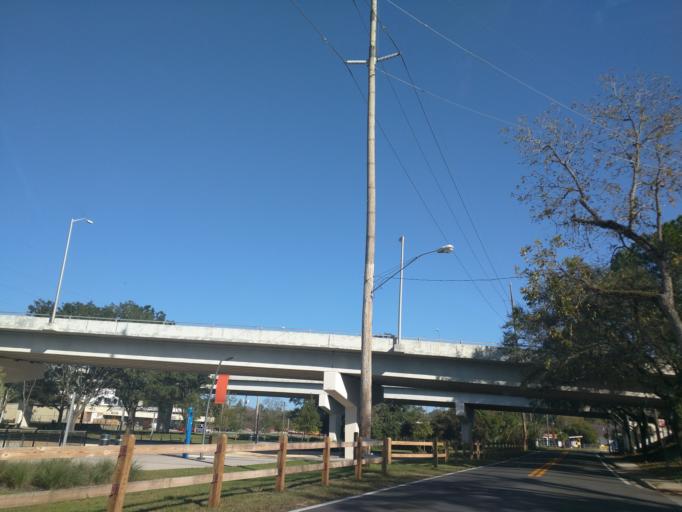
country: US
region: Florida
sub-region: Leon County
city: Tallahassee
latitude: 30.4317
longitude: -84.2839
